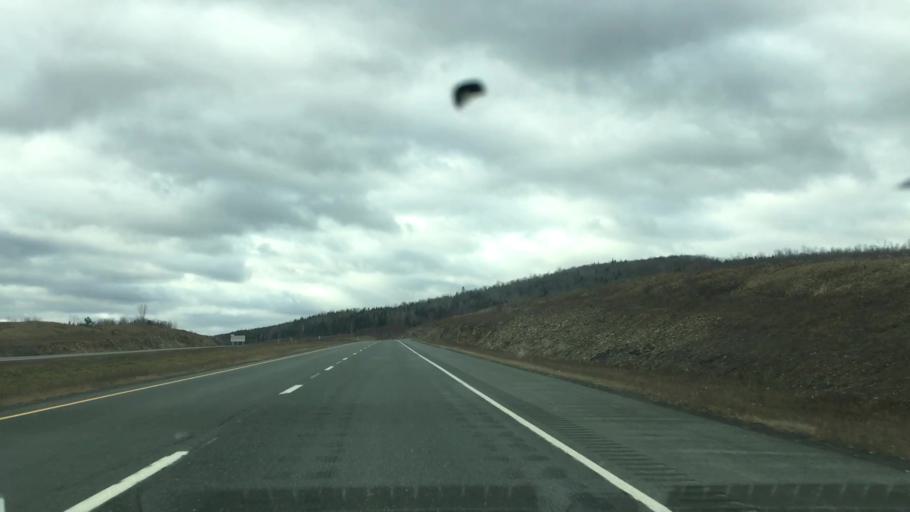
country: US
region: Maine
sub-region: Aroostook County
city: Fort Fairfield
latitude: 46.7306
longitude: -67.7230
